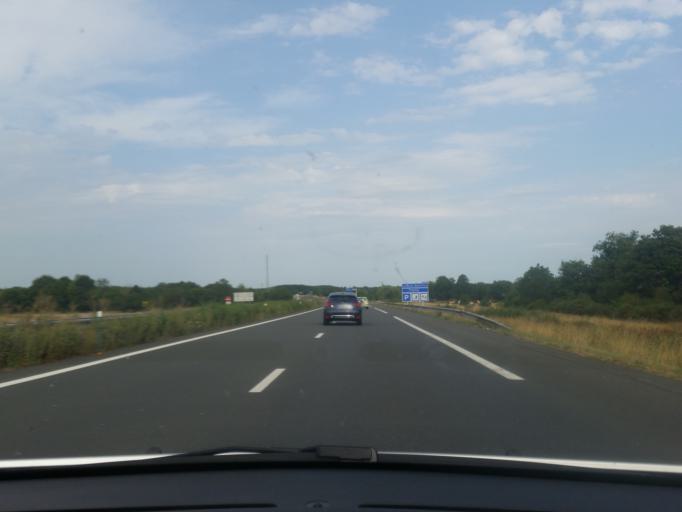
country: FR
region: Pays de la Loire
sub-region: Departement de Maine-et-Loire
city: Saint-Germain-des-Pres
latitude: 47.4337
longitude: -0.8018
